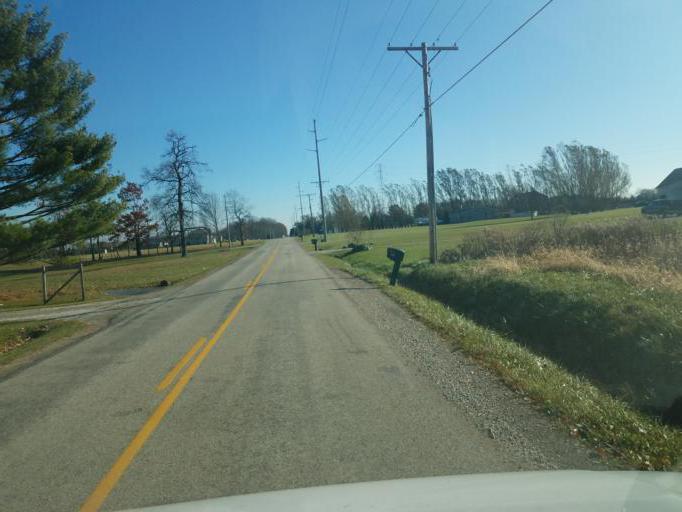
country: US
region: Ohio
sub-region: Ashland County
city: Ashland
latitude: 40.8289
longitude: -82.3394
